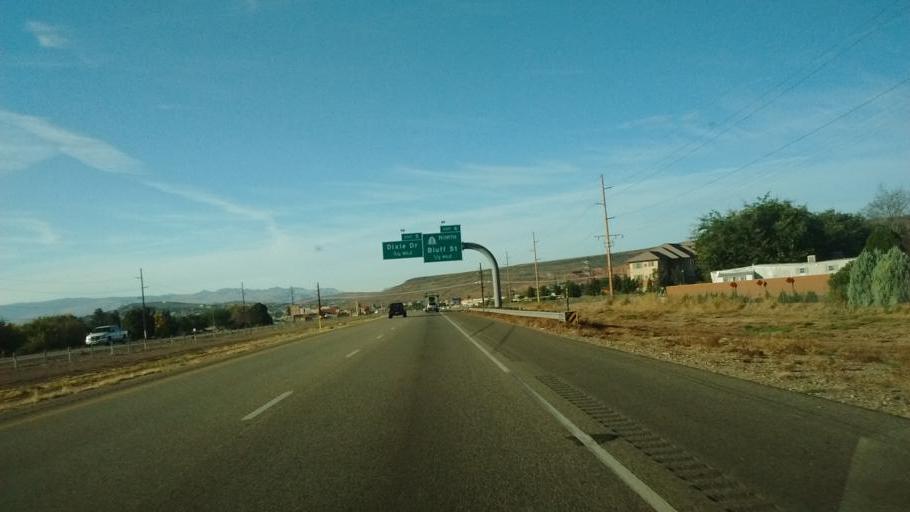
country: US
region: Utah
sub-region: Washington County
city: Saint George
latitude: 37.0927
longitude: -113.5716
